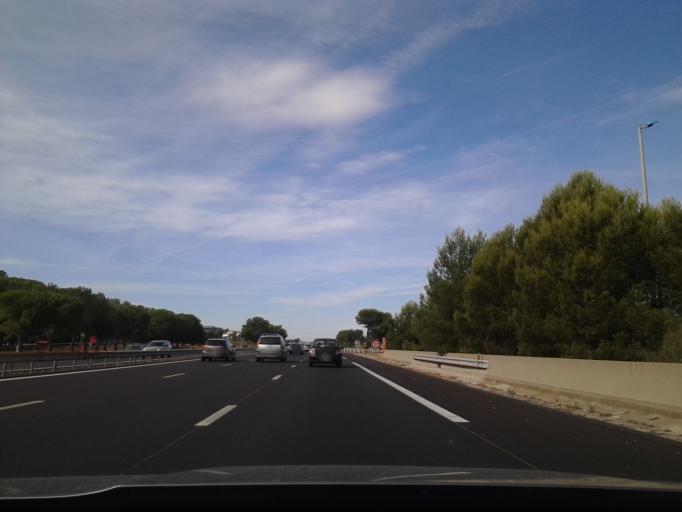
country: FR
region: Languedoc-Roussillon
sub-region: Departement de l'Herault
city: Fabregues
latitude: 43.5469
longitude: 3.7954
